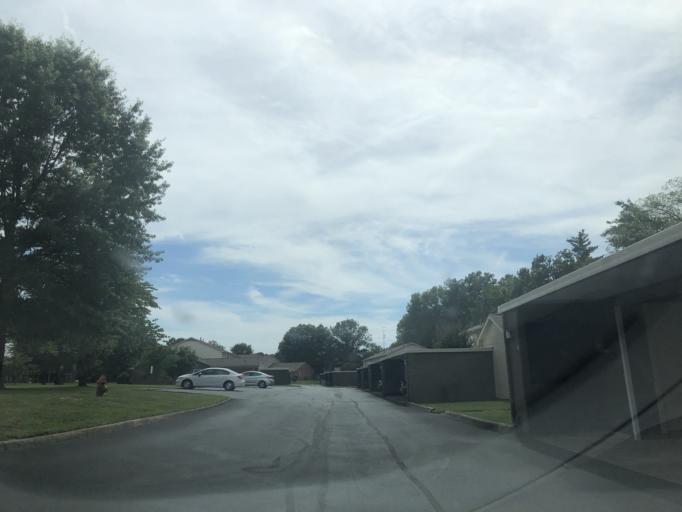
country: US
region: Tennessee
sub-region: Davidson County
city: Belle Meade
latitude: 36.0759
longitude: -86.9463
